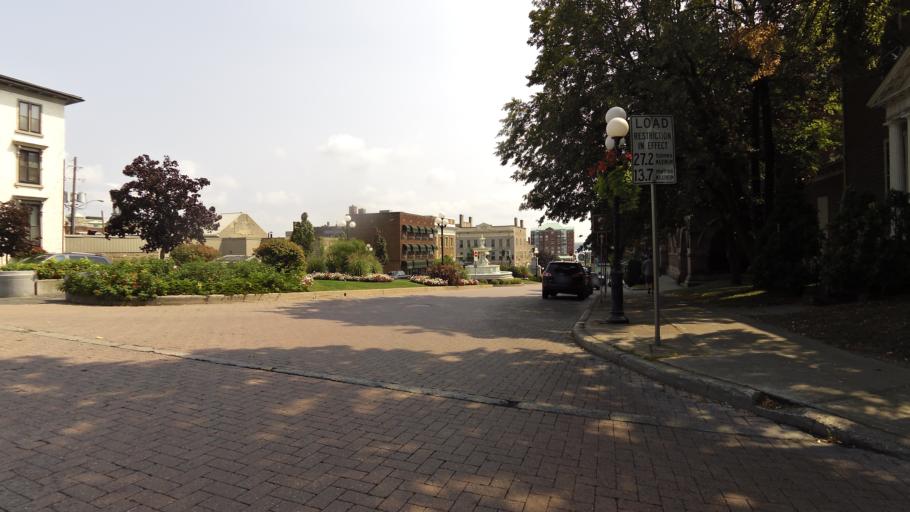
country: CA
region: Ontario
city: Brockville
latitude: 44.5902
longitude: -75.6853
